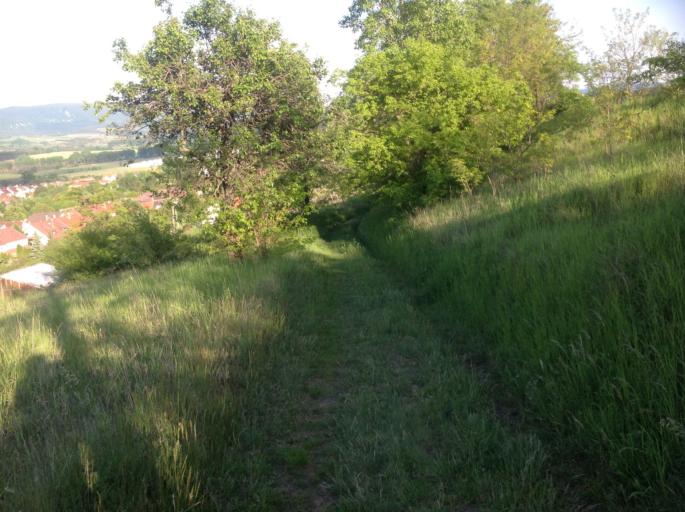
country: HU
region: Komarom-Esztergom
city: Dorog
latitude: 47.7150
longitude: 18.7286
